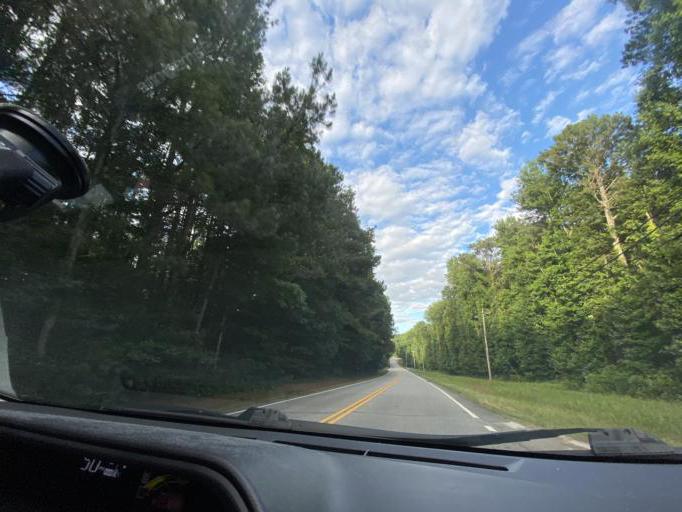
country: US
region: Georgia
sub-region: Fulton County
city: Palmetto
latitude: 33.4457
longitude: -84.6720
